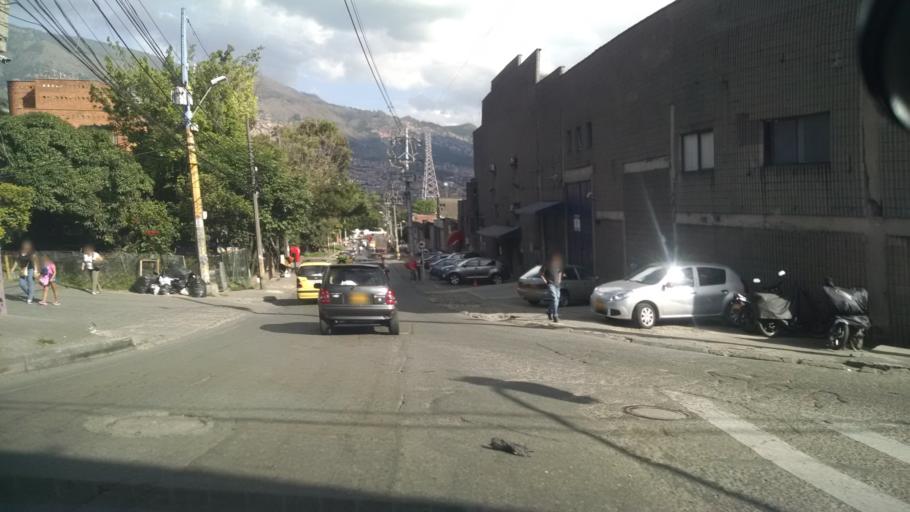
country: CO
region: Antioquia
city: Medellin
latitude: 6.2774
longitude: -75.5754
